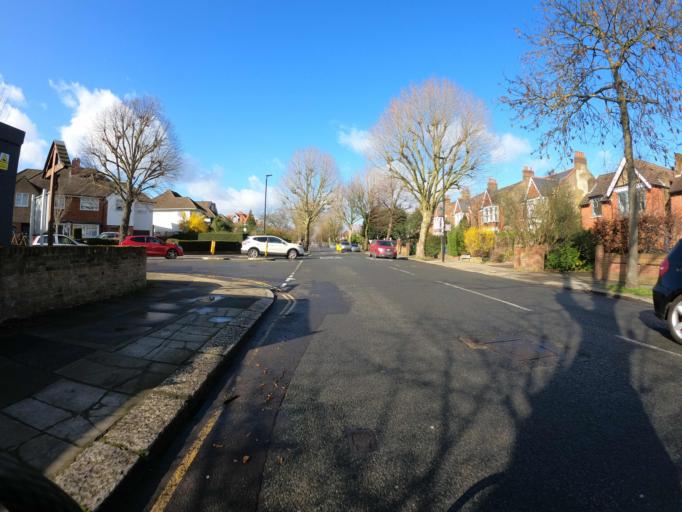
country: GB
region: England
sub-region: Greater London
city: Ealing
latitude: 51.5179
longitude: -0.3227
